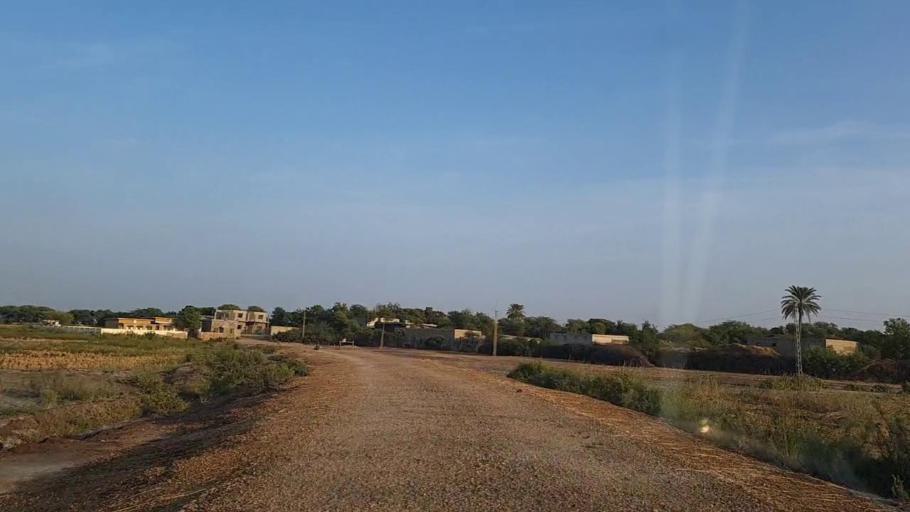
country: PK
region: Sindh
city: Daro Mehar
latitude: 24.6139
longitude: 68.0946
